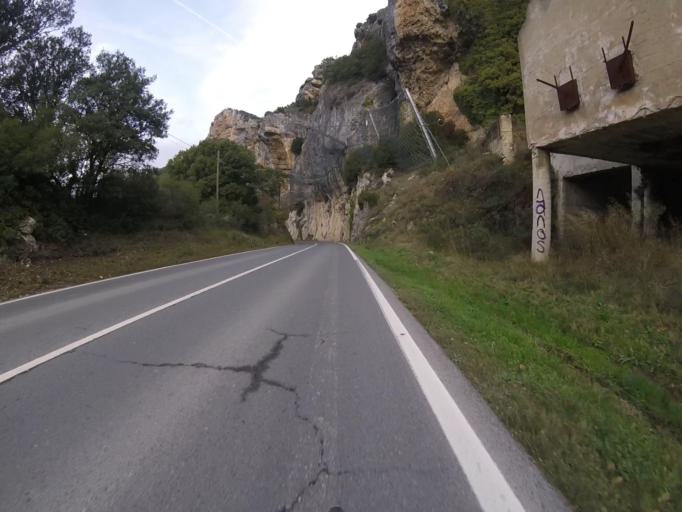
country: ES
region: Navarre
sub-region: Provincia de Navarra
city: Estella
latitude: 42.6994
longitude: -2.0564
